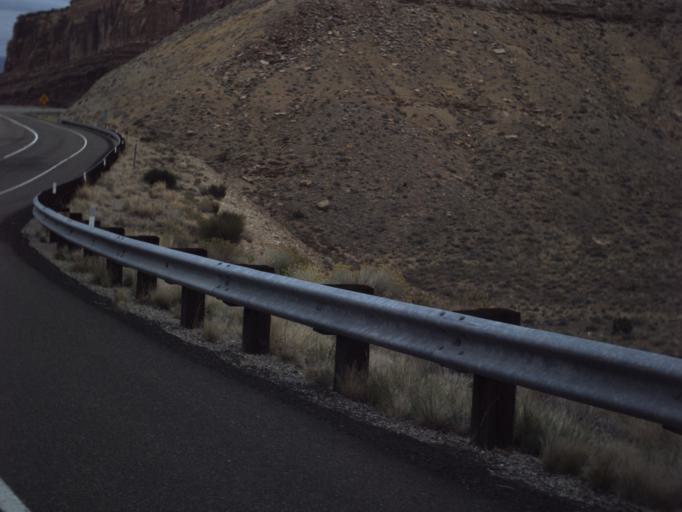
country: US
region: Utah
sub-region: Emery County
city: Castle Dale
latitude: 38.9363
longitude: -110.4769
